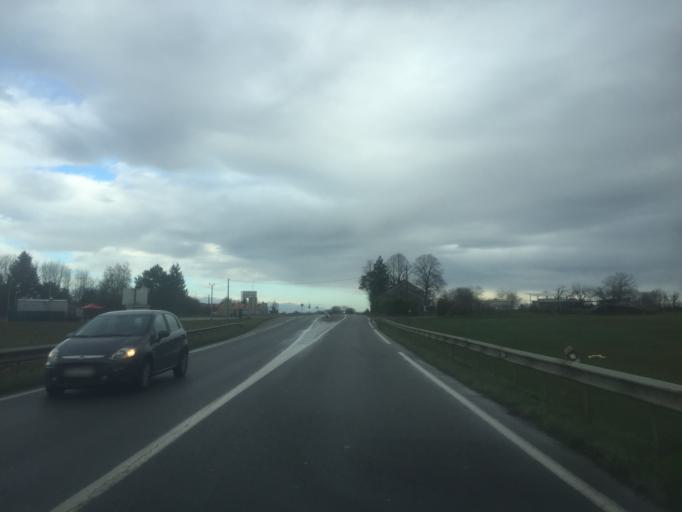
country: FR
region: Franche-Comte
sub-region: Departement du Jura
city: Fraisans
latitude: 47.1643
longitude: 5.7659
